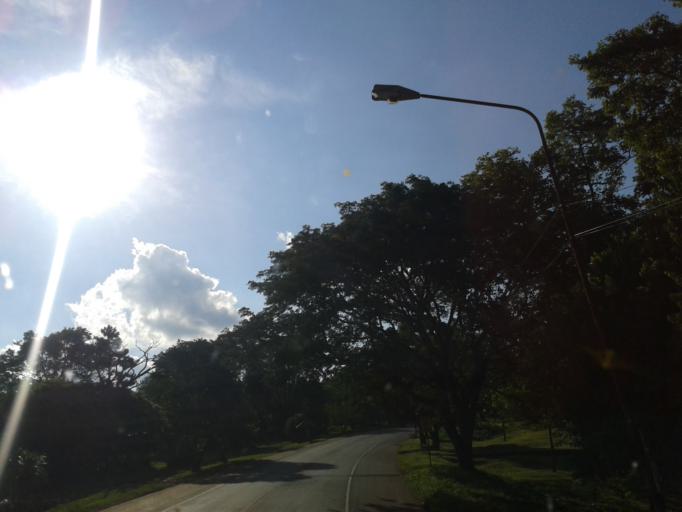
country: AR
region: Misiones
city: Guarani
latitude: -27.4952
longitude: -55.1668
